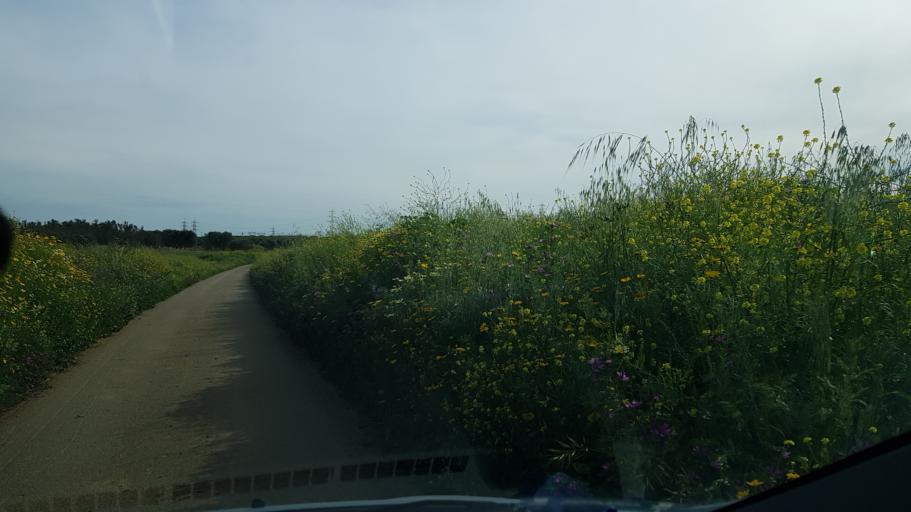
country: IT
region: Apulia
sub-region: Provincia di Brindisi
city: Tuturano
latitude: 40.5672
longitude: 17.9182
